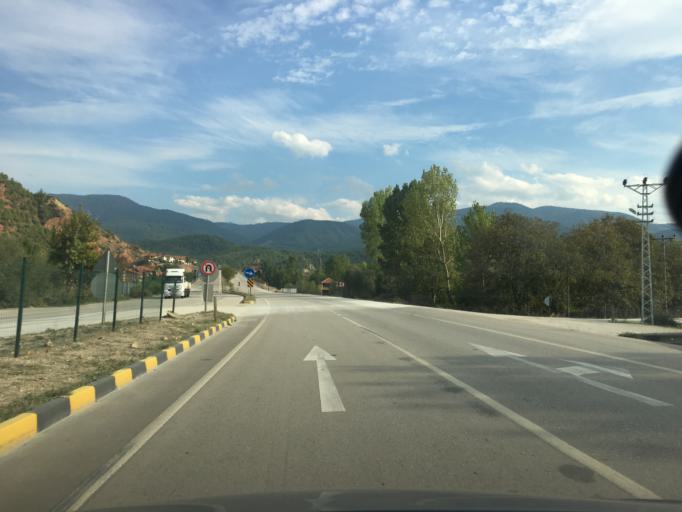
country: TR
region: Karabuk
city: Karabuk
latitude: 41.1006
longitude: 32.6706
